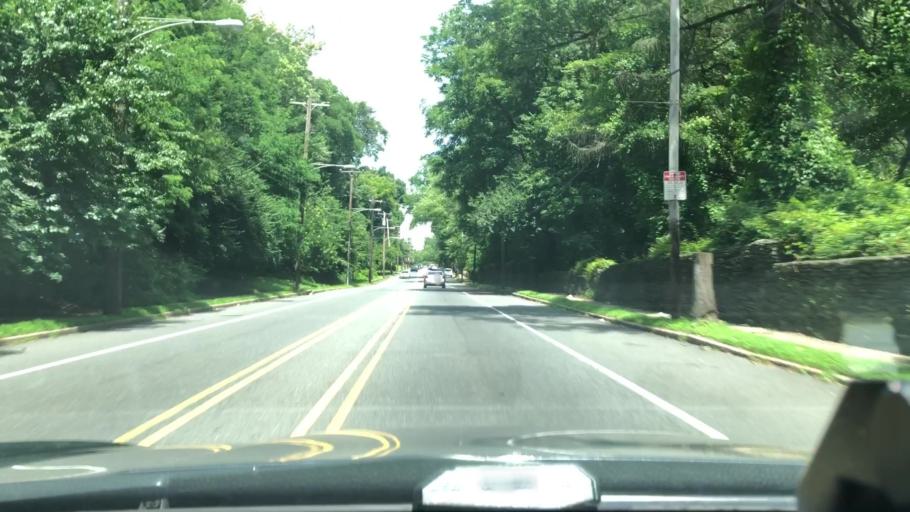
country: US
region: Pennsylvania
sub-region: Montgomery County
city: Wyndmoor
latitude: 40.0523
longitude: -75.1715
